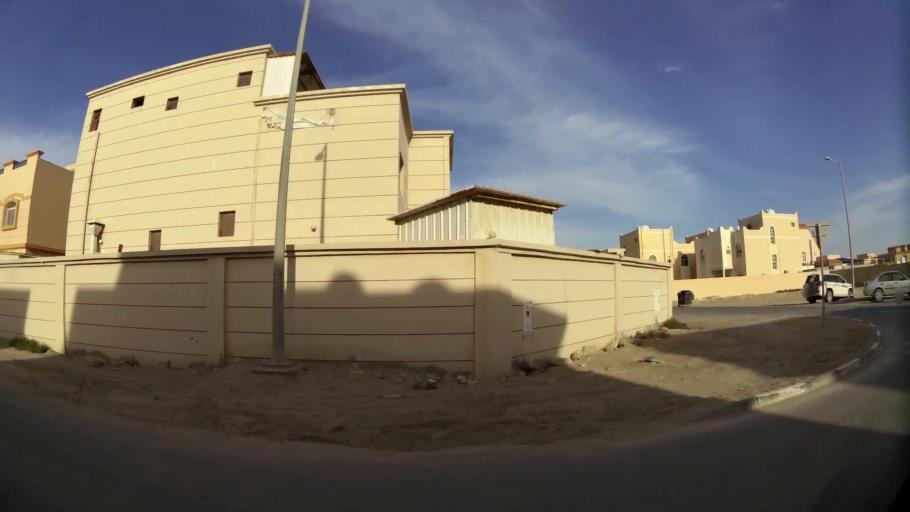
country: QA
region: Al Wakrah
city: Al Wakrah
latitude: 25.1428
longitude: 51.6140
